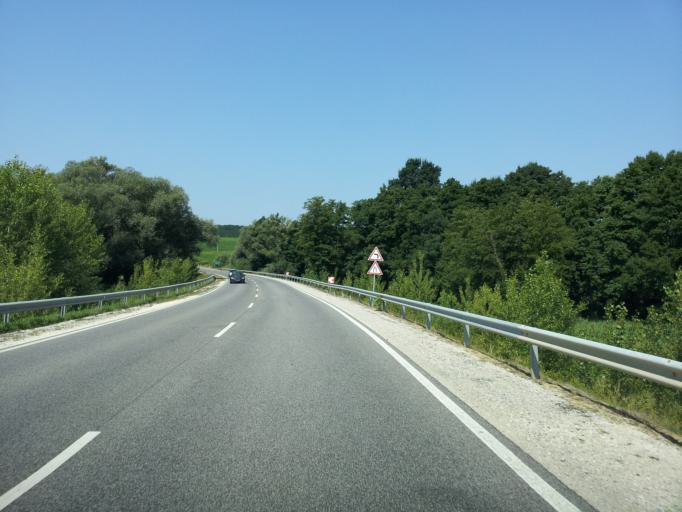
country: HU
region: Zala
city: Zalaszentgrot
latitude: 46.8363
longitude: 17.0340
